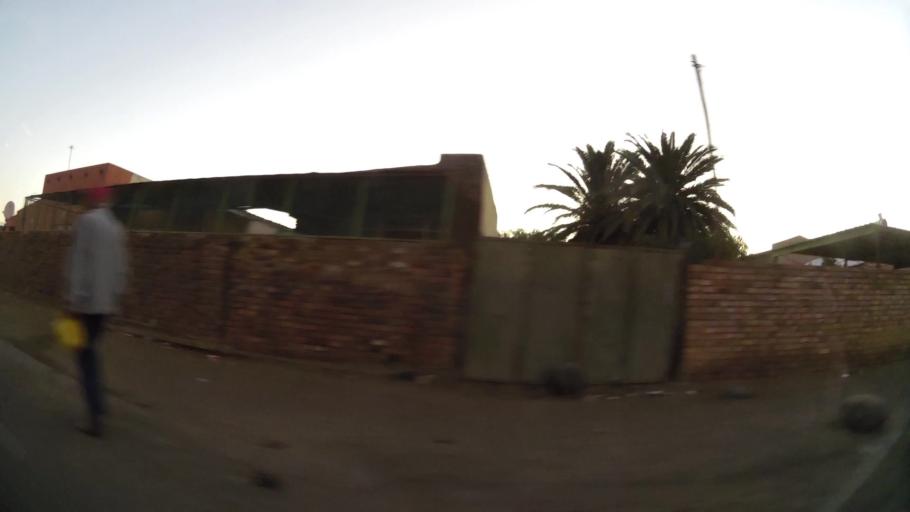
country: ZA
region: Northern Cape
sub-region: Frances Baard District Municipality
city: Kimberley
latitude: -28.7153
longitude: 24.7626
